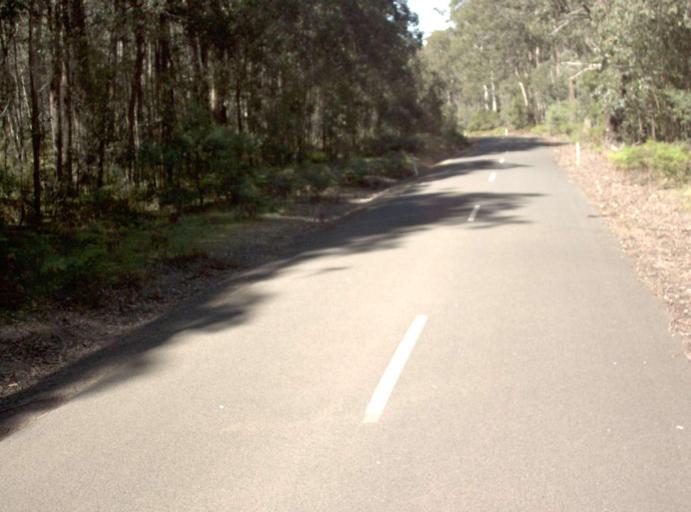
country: AU
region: New South Wales
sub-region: Bombala
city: Bombala
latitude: -37.0790
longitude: 148.7771
